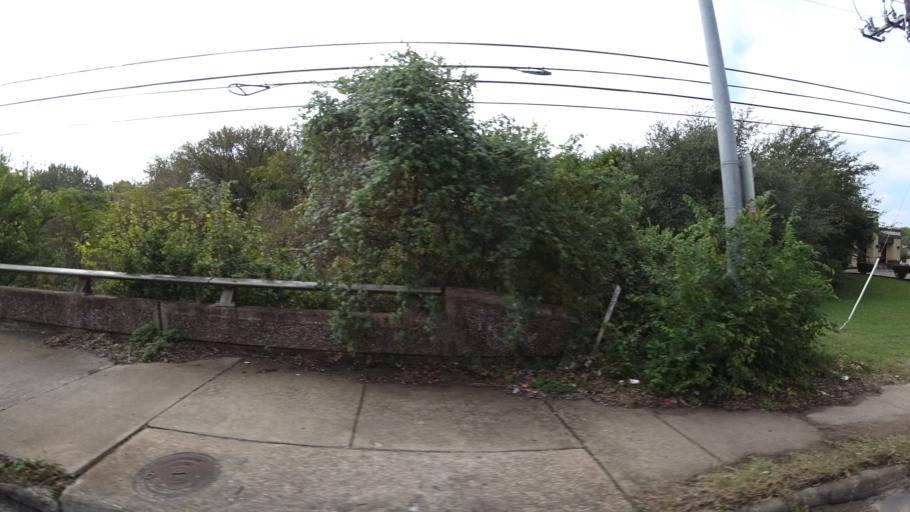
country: US
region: Texas
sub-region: Travis County
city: Shady Hollow
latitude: 30.2131
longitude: -97.8291
